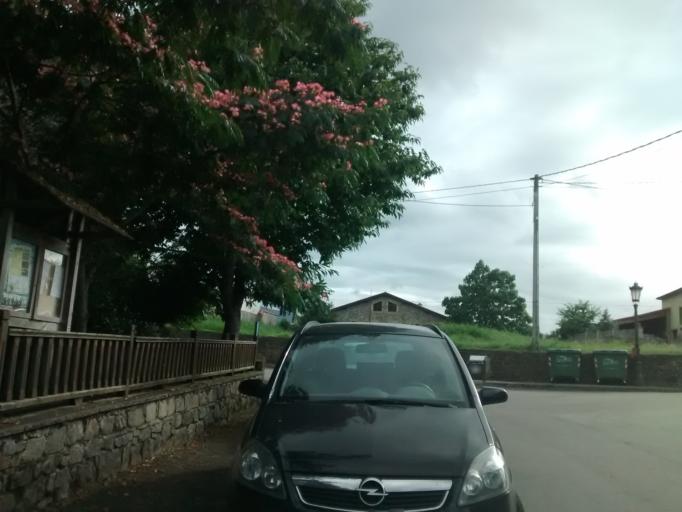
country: ES
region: Cantabria
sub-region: Provincia de Cantabria
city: Comillas
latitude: 43.3376
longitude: -4.3266
